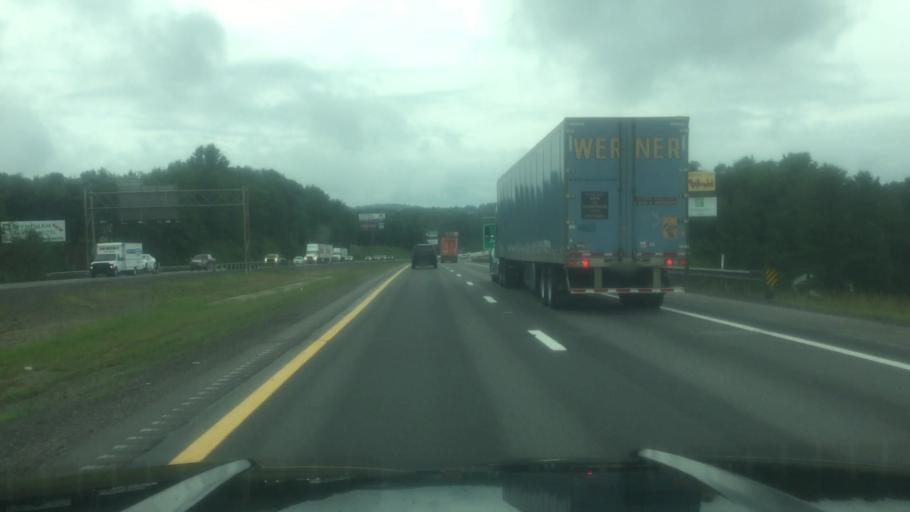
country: US
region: West Virginia
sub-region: Raleigh County
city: Mabscott
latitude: 37.7748
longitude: -81.2203
